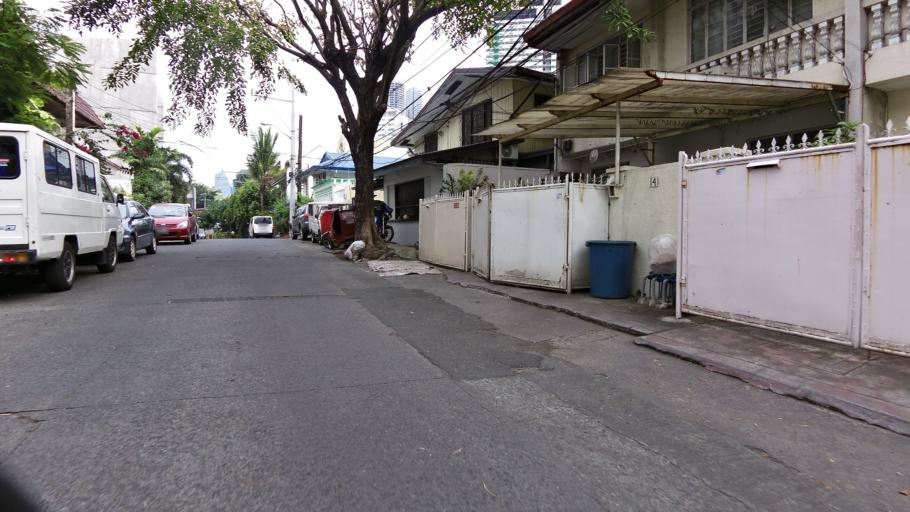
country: PH
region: Metro Manila
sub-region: Pasig
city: Pasig City
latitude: 14.5703
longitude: 121.0619
